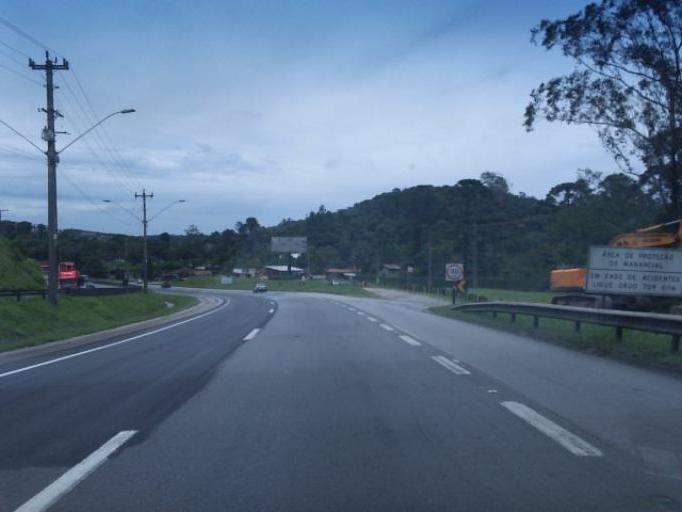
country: BR
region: Sao Paulo
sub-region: Sao Lourenco Da Serra
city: Sao Lourenco da Serra
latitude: -23.8445
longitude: -46.9362
